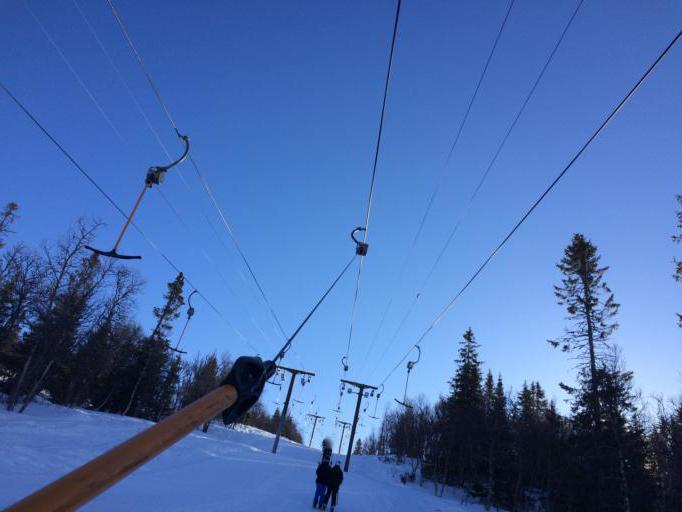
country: SE
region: Jaemtland
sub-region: Are Kommun
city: Are
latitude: 63.4304
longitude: 13.0168
